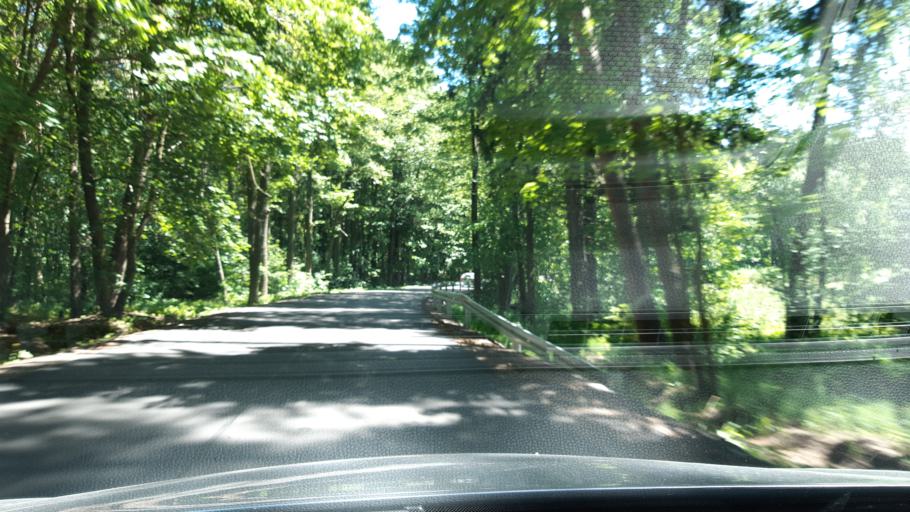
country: PL
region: Warmian-Masurian Voivodeship
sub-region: Powiat gizycki
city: Gizycko
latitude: 53.9546
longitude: 21.7372
